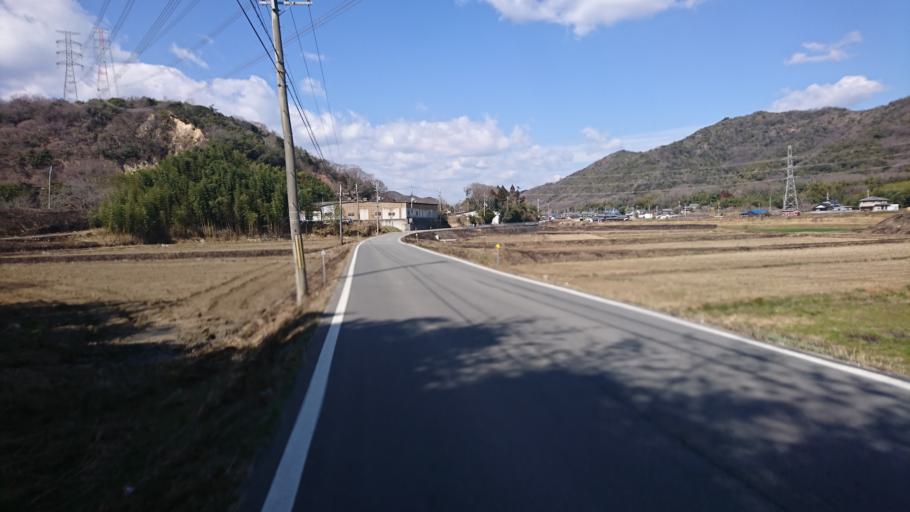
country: JP
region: Hyogo
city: Kakogawacho-honmachi
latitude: 34.8380
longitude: 134.8209
